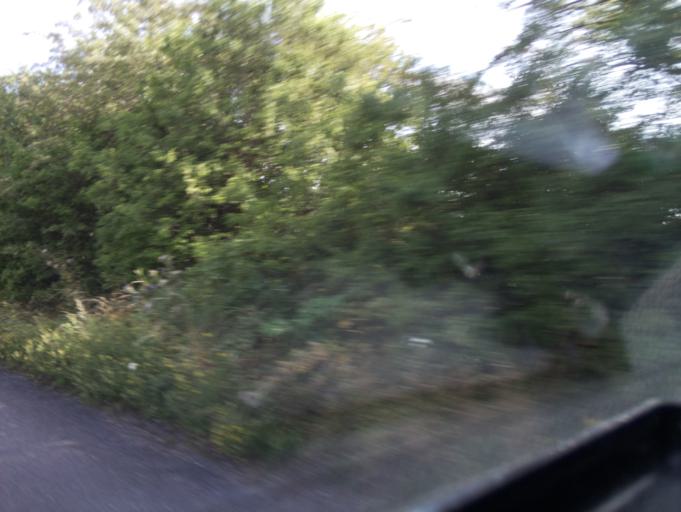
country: GB
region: England
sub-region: Gloucestershire
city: Cirencester
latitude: 51.7366
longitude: -1.9869
